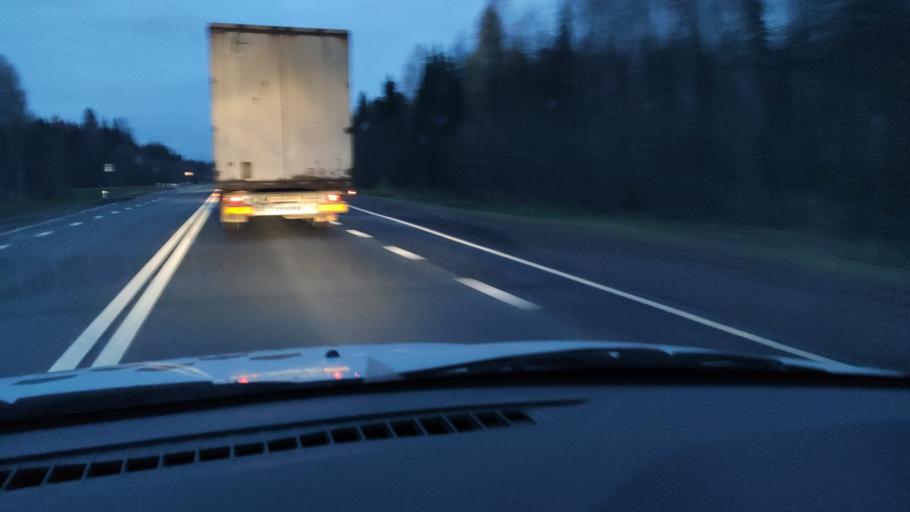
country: RU
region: Kirov
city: Kostino
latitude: 58.8316
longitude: 53.4589
